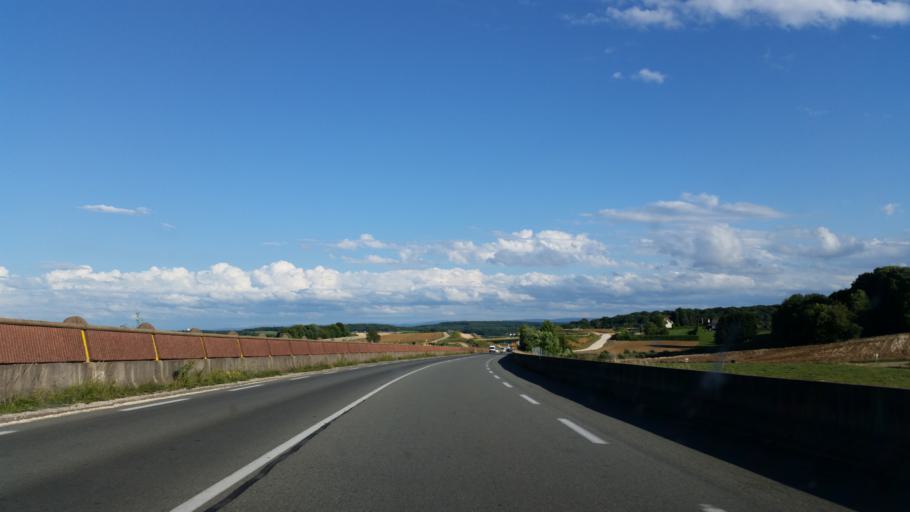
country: FR
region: Franche-Comte
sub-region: Territoire de Belfort
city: Andelnans
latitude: 47.5970
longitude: 6.8412
